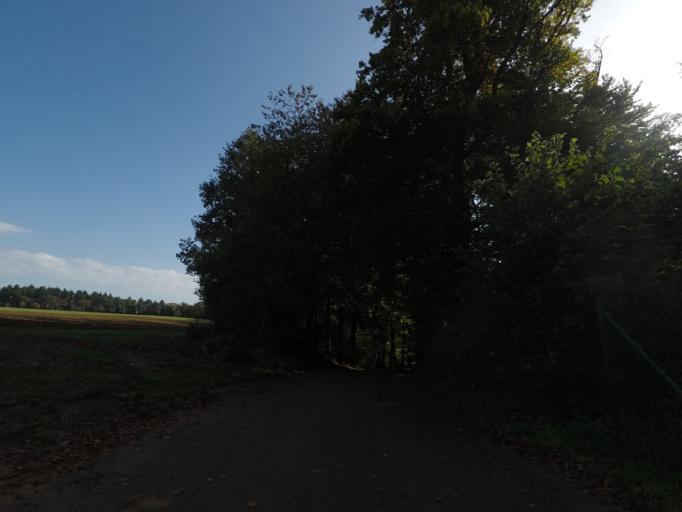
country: LU
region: Luxembourg
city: Itzig
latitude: 49.5961
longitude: 6.1733
